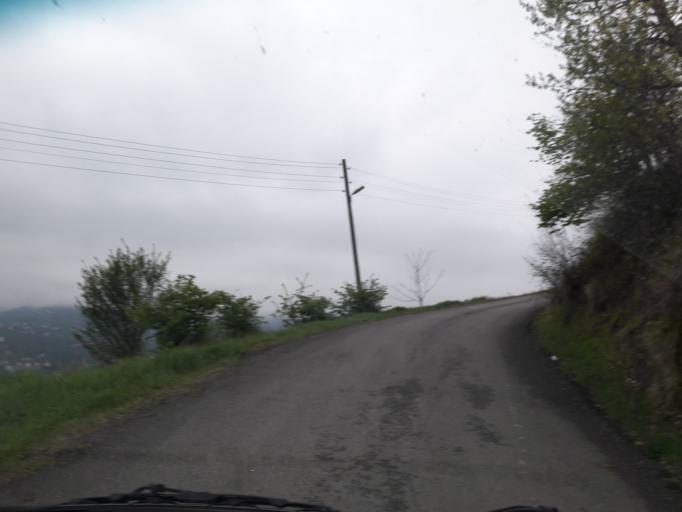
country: TR
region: Trabzon
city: Duzkoy
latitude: 40.9319
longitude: 39.4779
